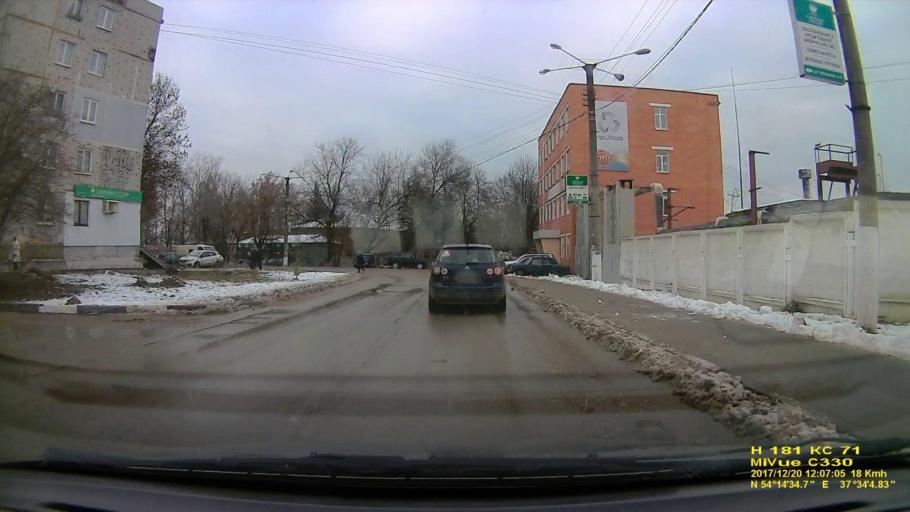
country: RU
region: Tula
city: Gorelki
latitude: 54.2430
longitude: 37.5681
